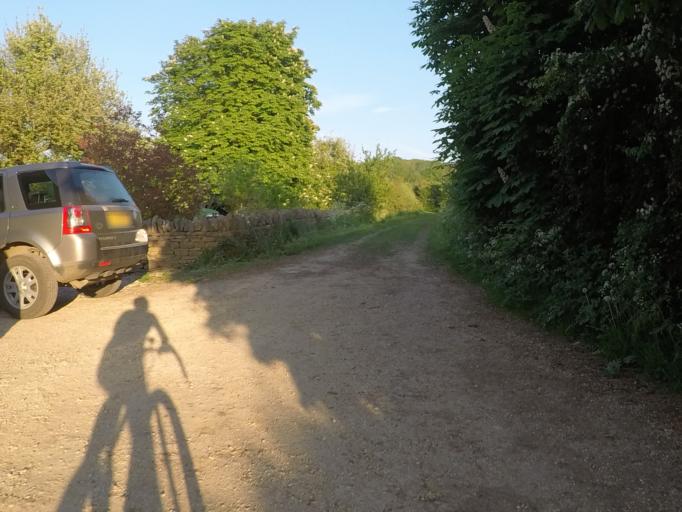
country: GB
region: England
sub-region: Oxfordshire
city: Charlbury
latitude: 51.8680
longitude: -1.5360
